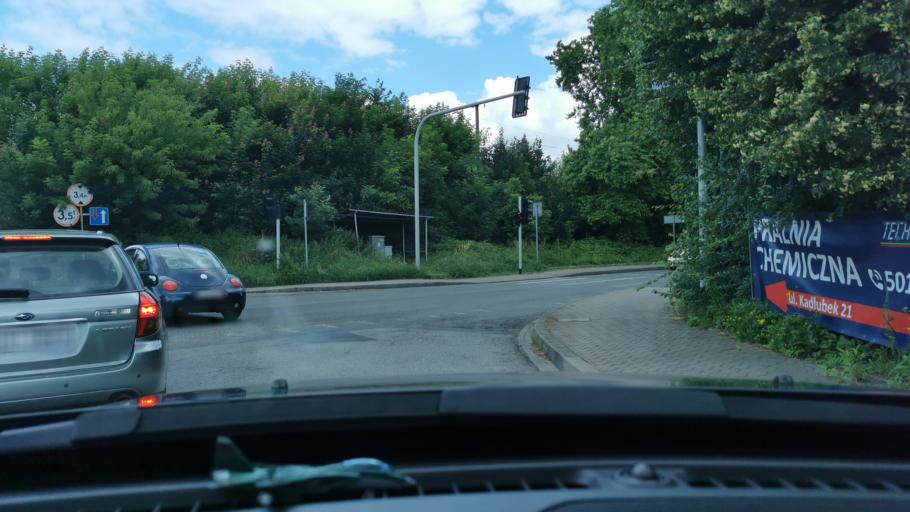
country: PL
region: Lesser Poland Voivodeship
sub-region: Powiat chrzanowski
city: Chrzanow
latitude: 50.1383
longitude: 19.4068
